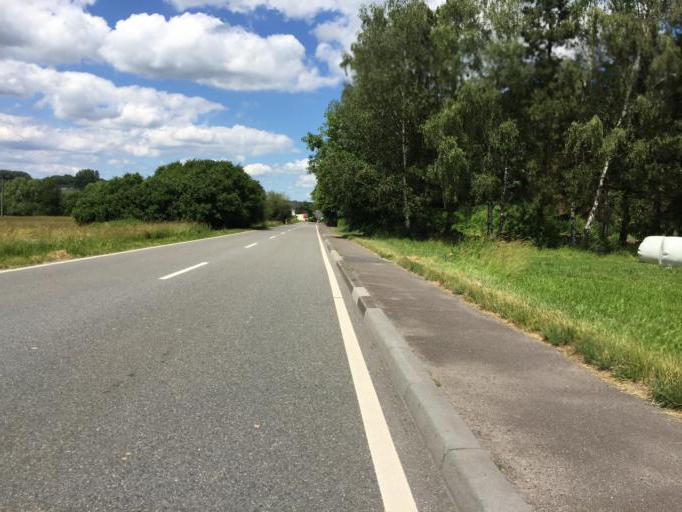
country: DE
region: Rheinland-Pfalz
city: Bannberscheid
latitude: 50.4668
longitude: 7.8400
